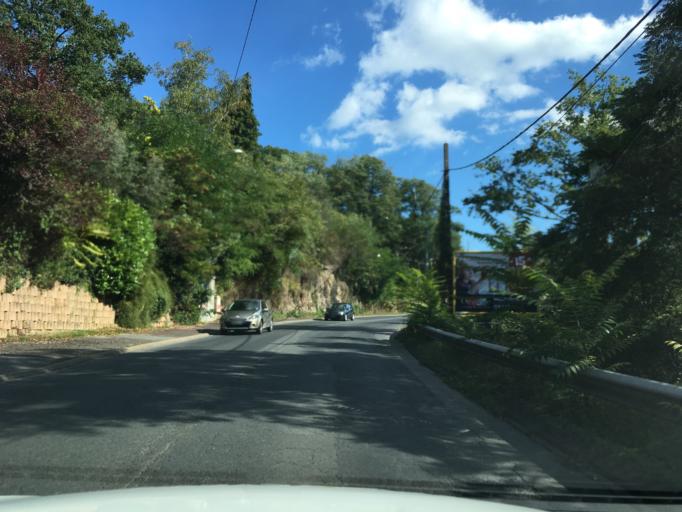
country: FR
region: Limousin
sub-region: Departement de la Correze
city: Brive-la-Gaillarde
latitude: 45.1462
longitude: 1.5465
